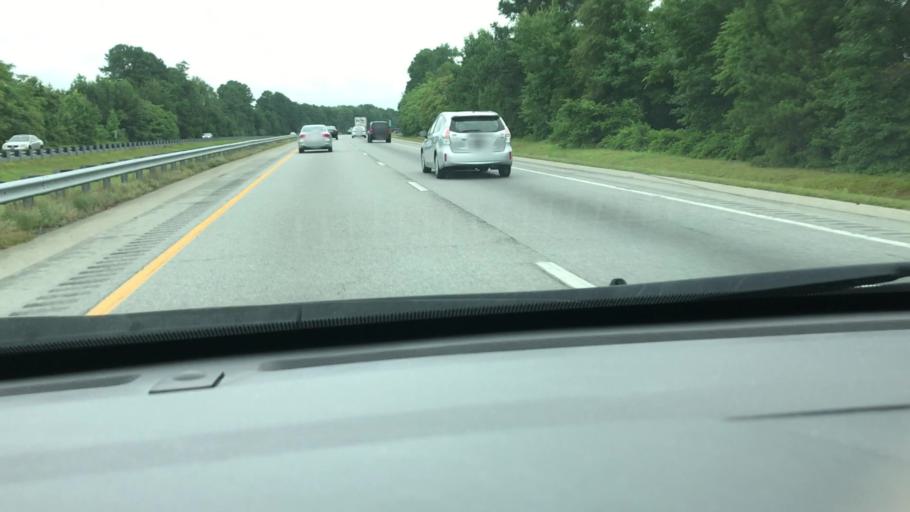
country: US
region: North Carolina
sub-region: Northampton County
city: Gaston
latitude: 36.4986
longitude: -77.5977
